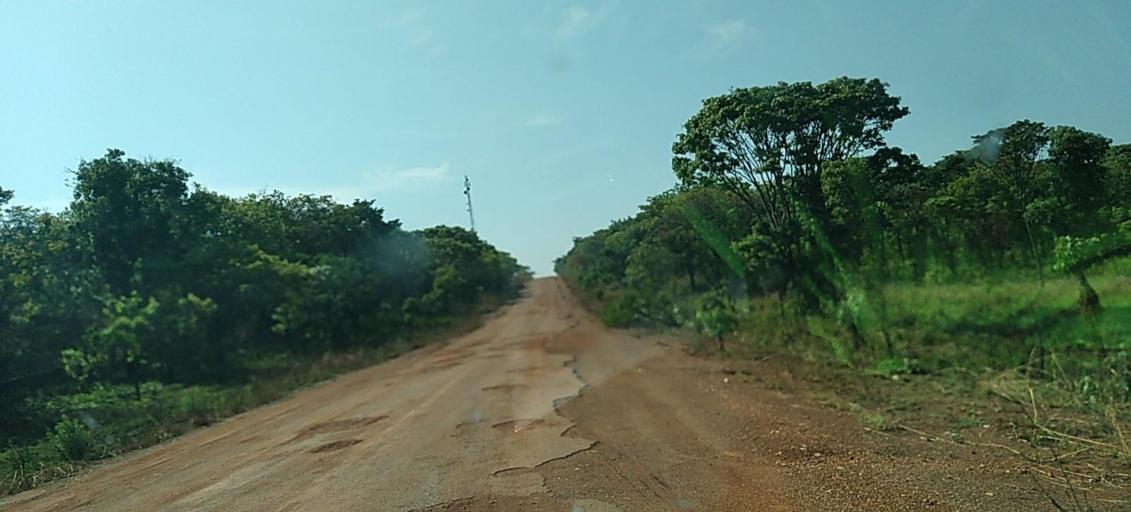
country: ZM
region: North-Western
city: Mwinilunga
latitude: -11.8076
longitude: 25.0818
